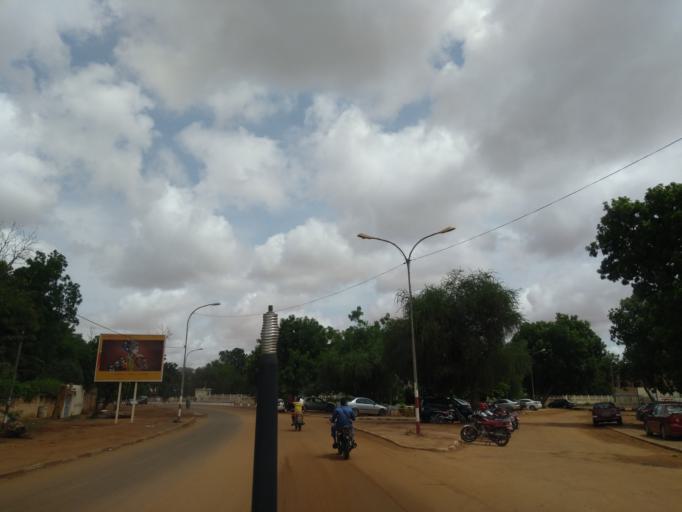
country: NE
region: Niamey
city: Niamey
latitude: 13.5197
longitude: 2.0955
